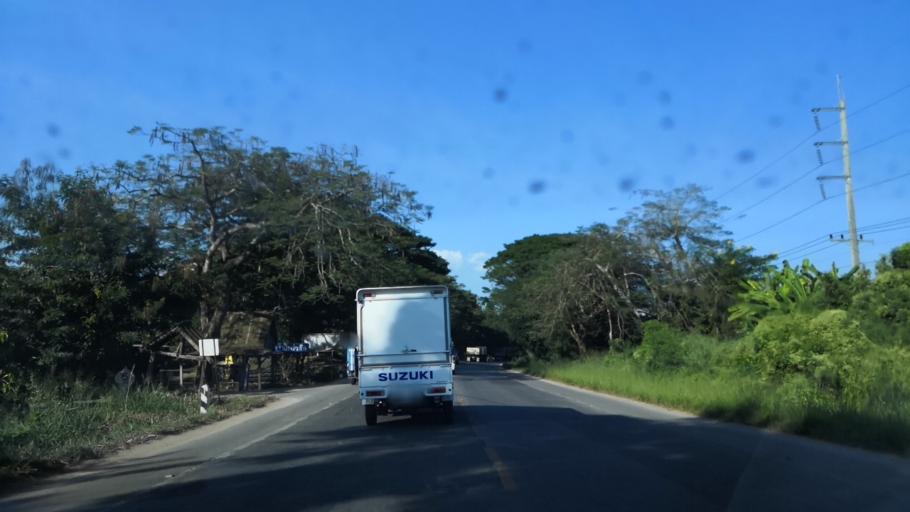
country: TH
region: Chiang Rai
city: Mae Suai
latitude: 19.5191
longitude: 99.4791
